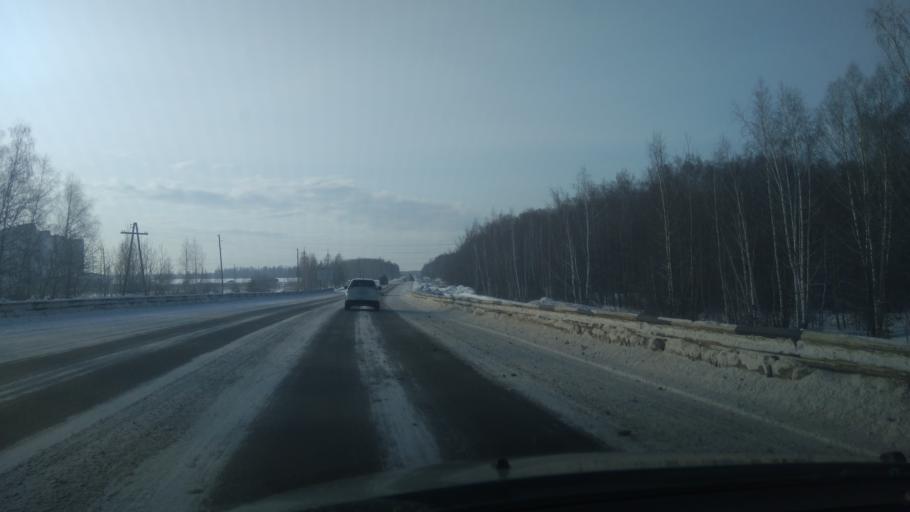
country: RU
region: Sverdlovsk
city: Bogdanovich
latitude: 56.8100
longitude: 62.0388
